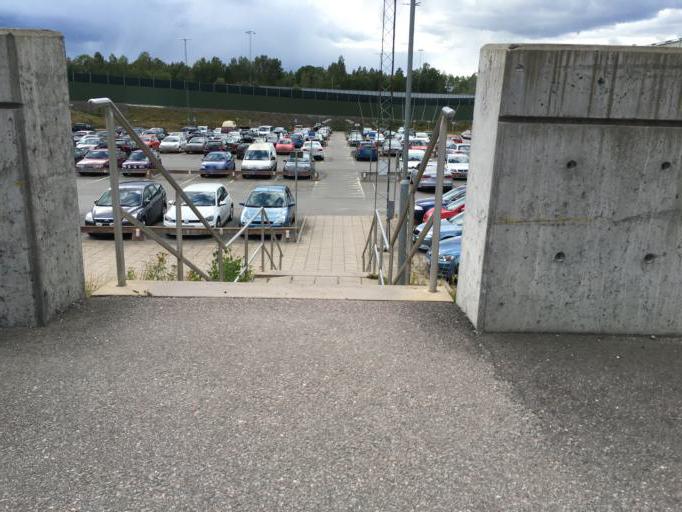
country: SE
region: Stockholm
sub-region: Sodertalje Kommun
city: Pershagen
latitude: 59.1668
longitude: 17.6350
